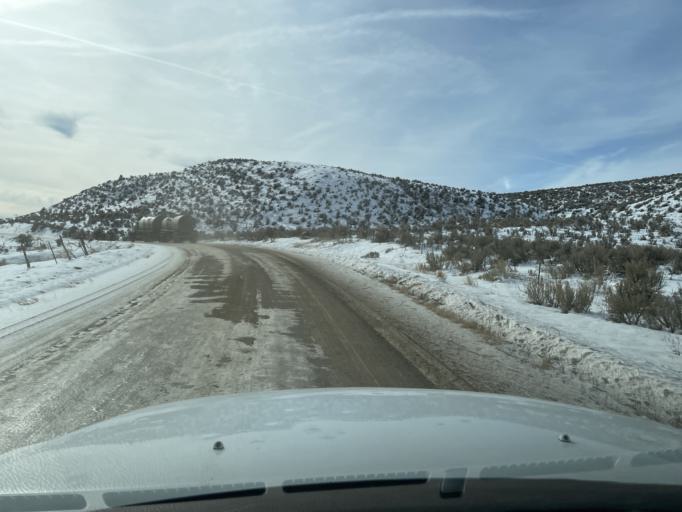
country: US
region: Colorado
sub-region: Moffat County
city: Craig
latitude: 40.3337
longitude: -107.6882
